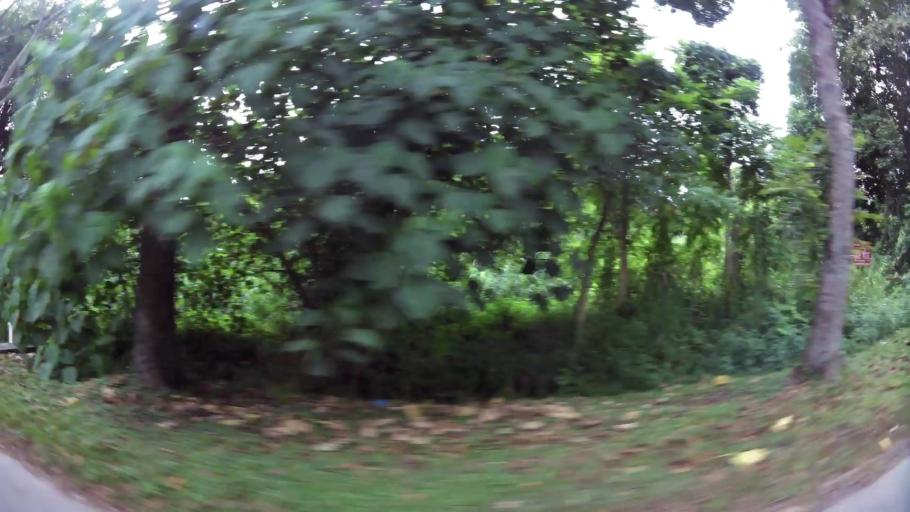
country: MY
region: Johor
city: Johor Bahru
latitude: 1.4245
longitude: 103.7045
